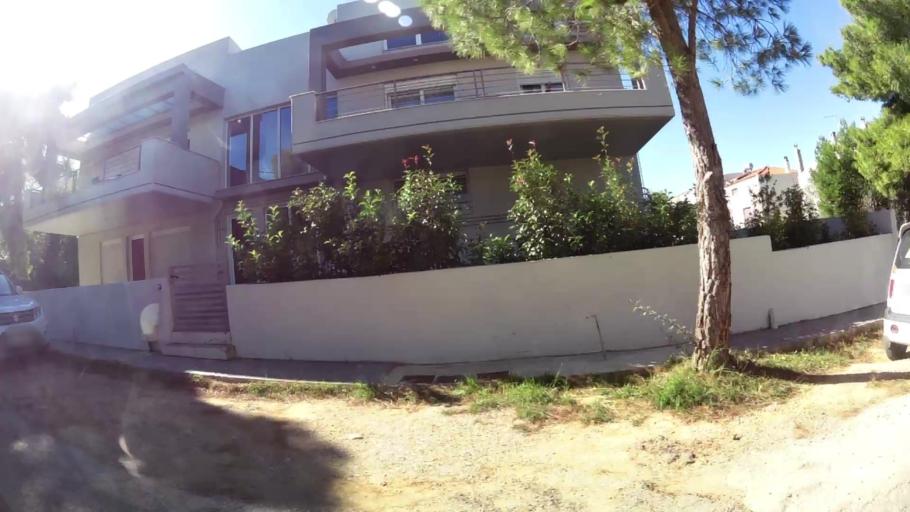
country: GR
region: Attica
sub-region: Nomarchia Athinas
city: Nea Erythraia
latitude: 38.0962
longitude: 23.7886
